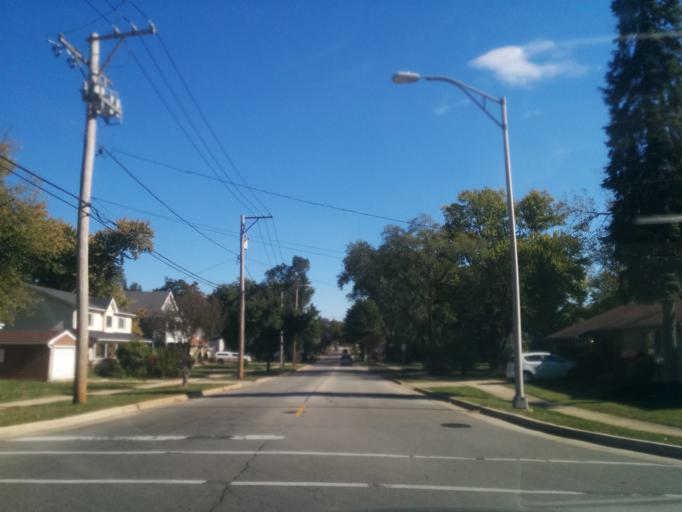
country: US
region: Illinois
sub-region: DuPage County
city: Lombard
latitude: 41.8744
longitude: -88.0293
